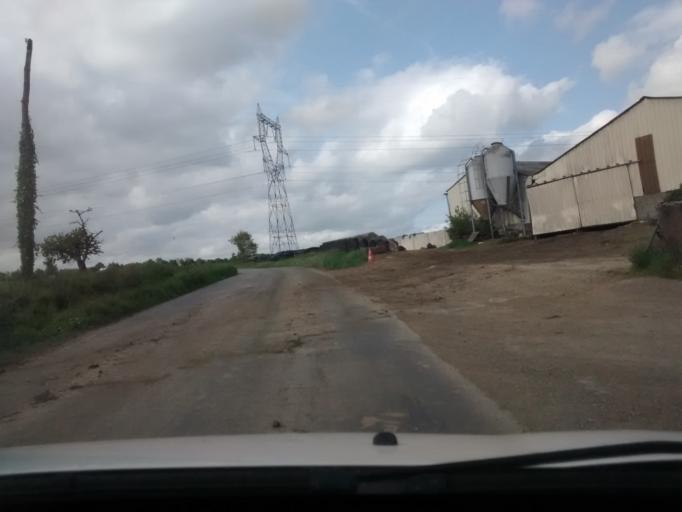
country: FR
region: Brittany
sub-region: Departement d'Ille-et-Vilaine
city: Nouvoitou
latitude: 48.0799
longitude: -1.5467
